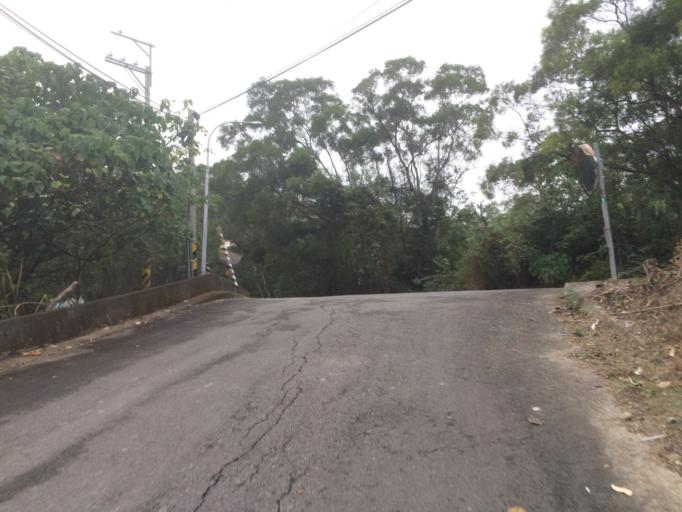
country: TW
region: Taiwan
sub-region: Taichung City
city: Taichung
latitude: 24.1607
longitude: 120.7591
